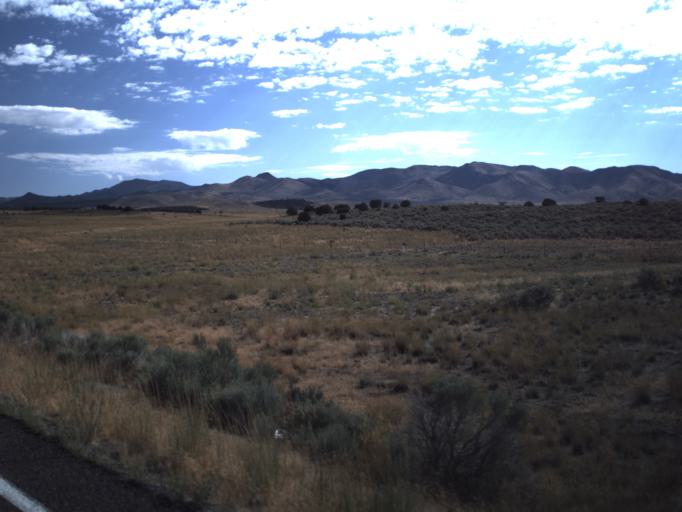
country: US
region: Utah
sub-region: Juab County
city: Mona
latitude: 39.7274
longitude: -112.1955
